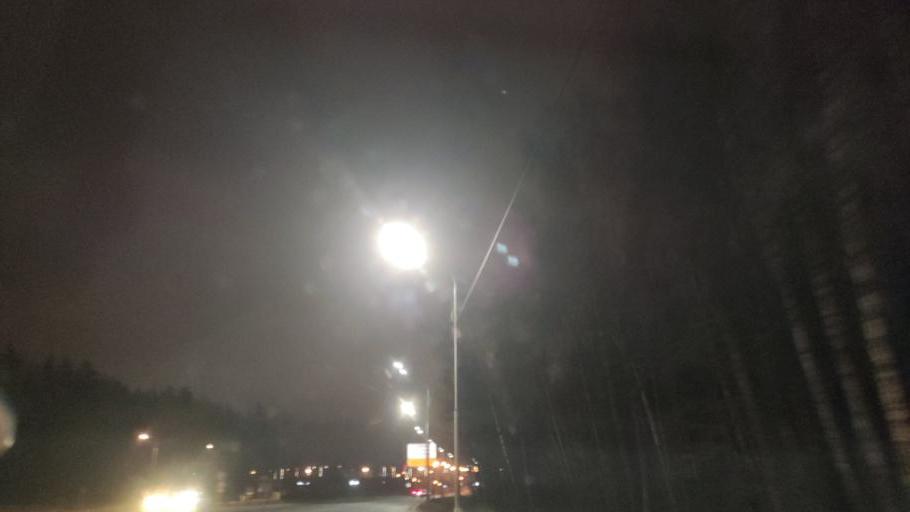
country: RU
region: Moskovskaya
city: Moskovskiy
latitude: 55.6146
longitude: 37.3468
